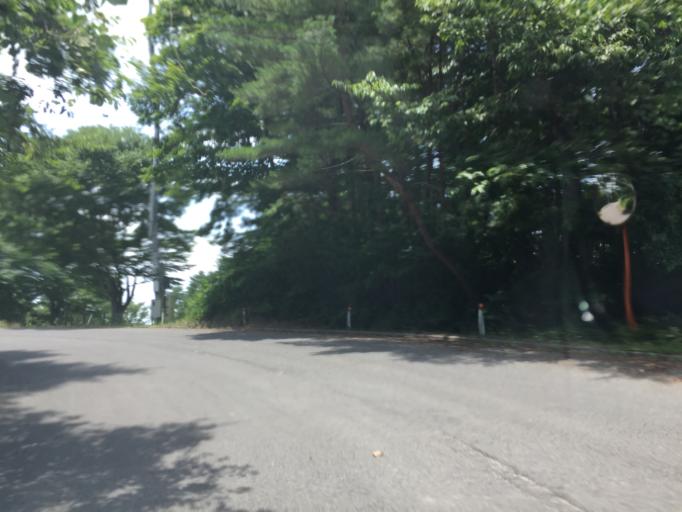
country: JP
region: Fukushima
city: Hobaramachi
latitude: 37.6806
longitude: 140.6560
